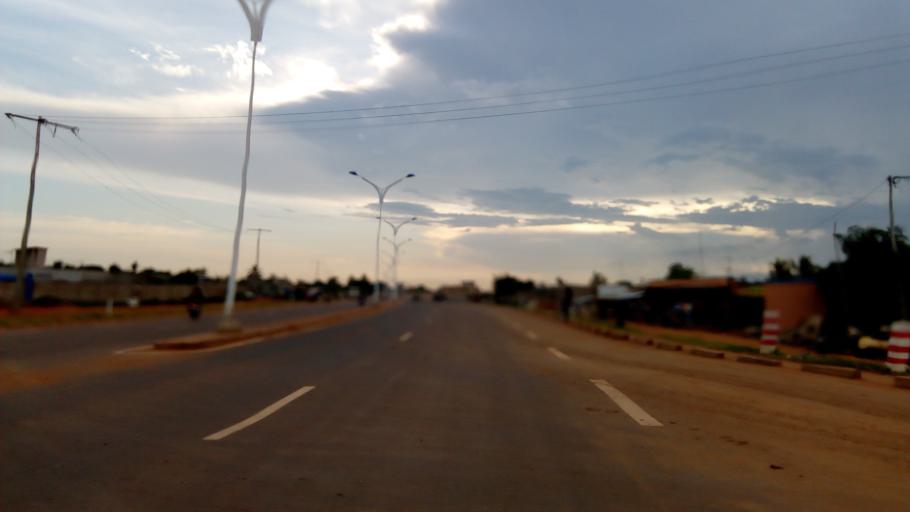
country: TG
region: Maritime
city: Lome
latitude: 6.2669
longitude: 1.1495
